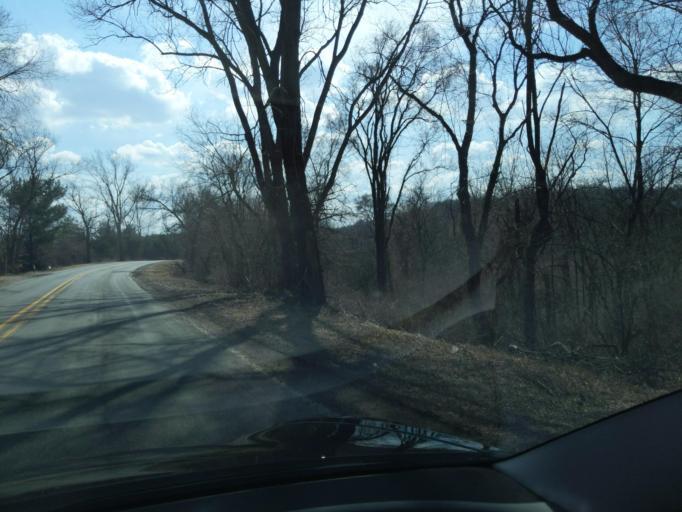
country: US
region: Michigan
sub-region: Washtenaw County
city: Chelsea
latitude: 42.4036
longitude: -84.0409
